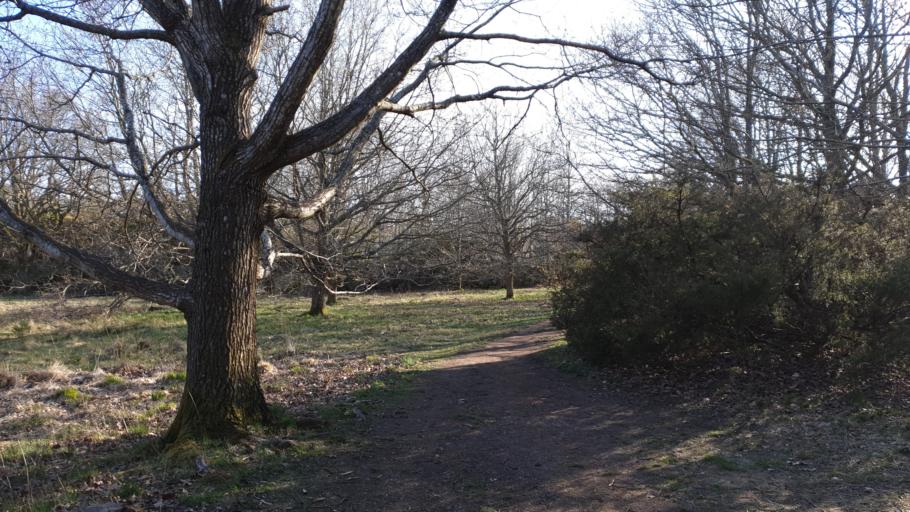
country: SE
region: Vaestra Goetaland
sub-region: Goteborg
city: Billdal
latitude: 57.5894
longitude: 11.9167
